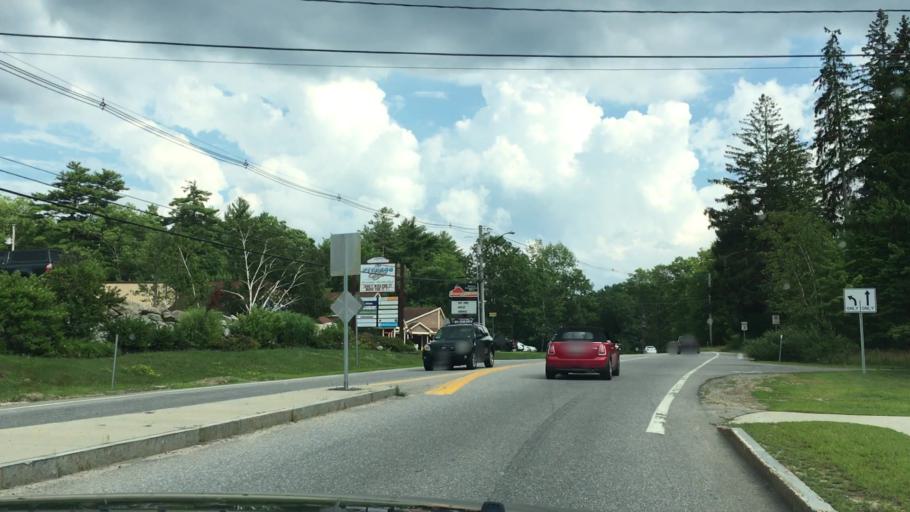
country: US
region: New Hampshire
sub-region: Belknap County
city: Meredith
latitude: 43.6400
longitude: -71.4991
